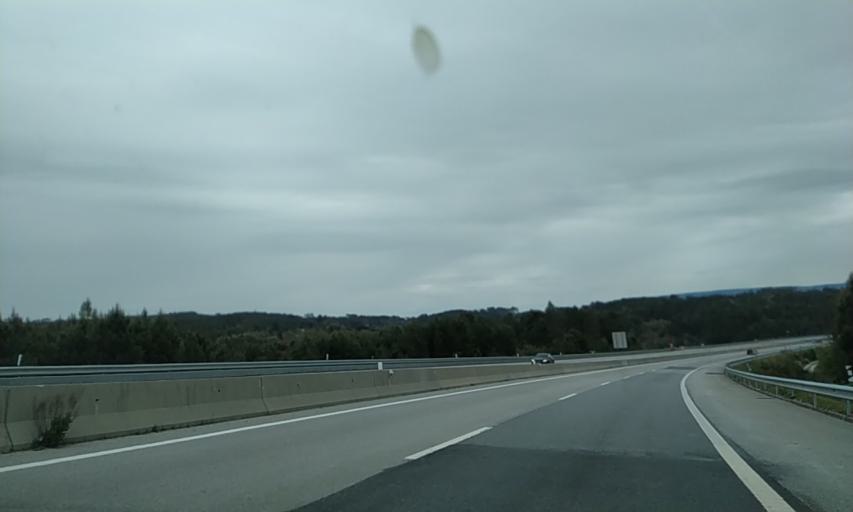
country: PT
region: Guarda
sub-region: Fornos de Algodres
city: Fornos de Algodres
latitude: 40.6195
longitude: -7.5788
